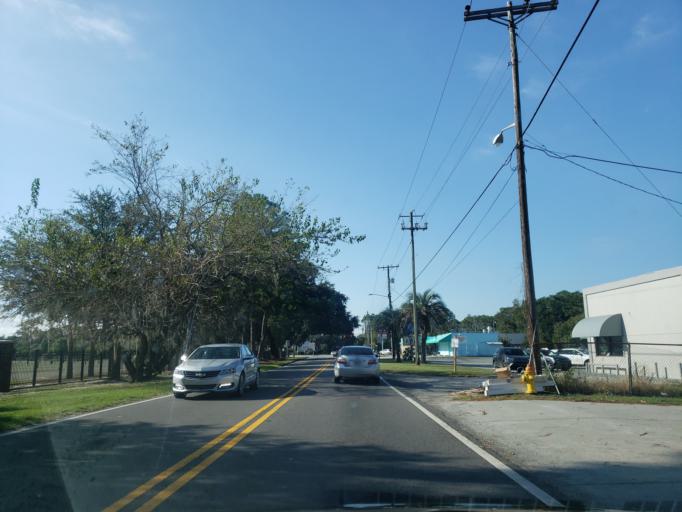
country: US
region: Georgia
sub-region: Chatham County
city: Thunderbolt
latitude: 32.0290
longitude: -81.0699
